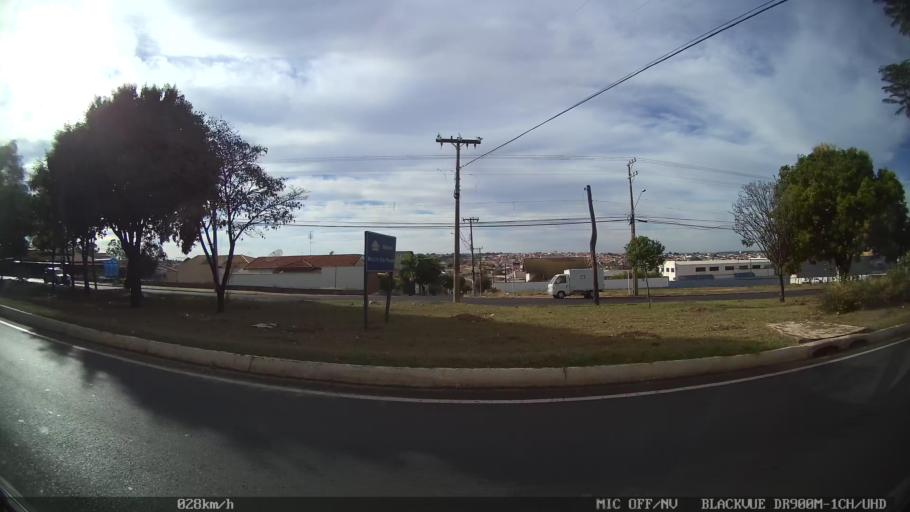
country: BR
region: Sao Paulo
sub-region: Catanduva
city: Catanduva
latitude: -21.1146
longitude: -48.9631
